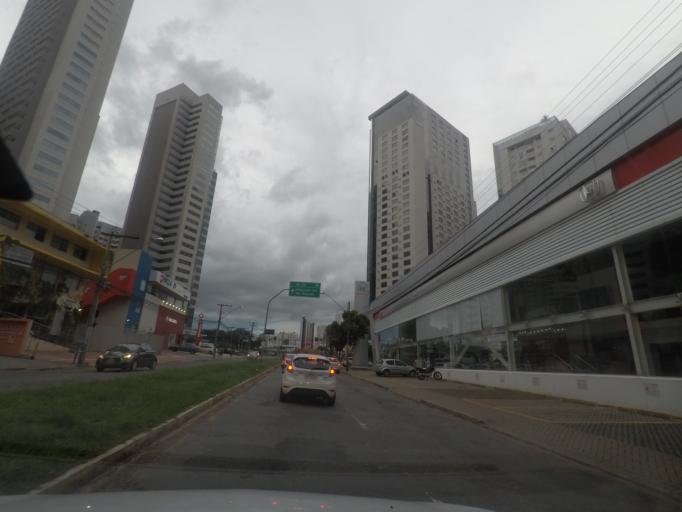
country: BR
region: Goias
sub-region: Goiania
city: Goiania
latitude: -16.7038
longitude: -49.2410
